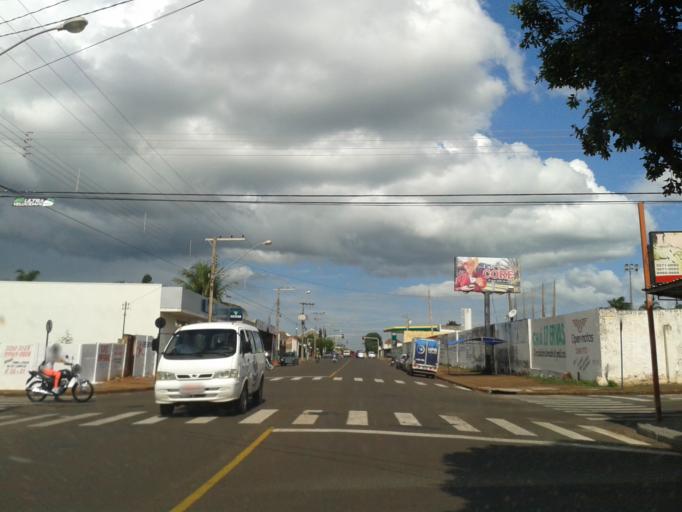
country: BR
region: Minas Gerais
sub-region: Ituiutaba
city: Ituiutaba
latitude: -18.9829
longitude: -49.4619
